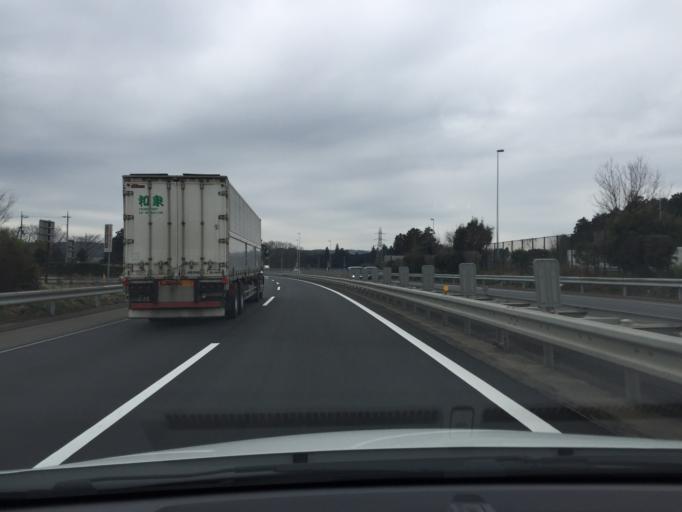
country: JP
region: Saitama
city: Sayama
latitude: 35.8520
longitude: 139.3663
